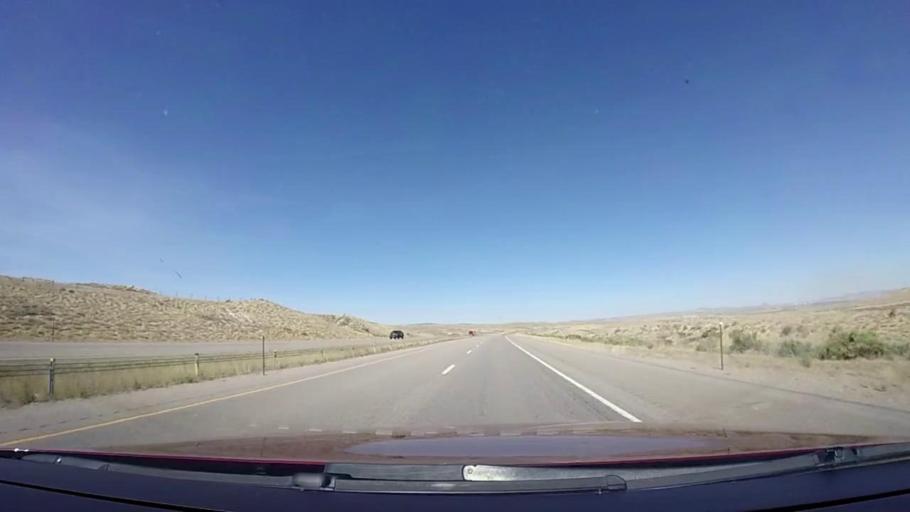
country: US
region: Wyoming
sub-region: Sweetwater County
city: Rock Springs
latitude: 41.6492
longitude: -108.6955
